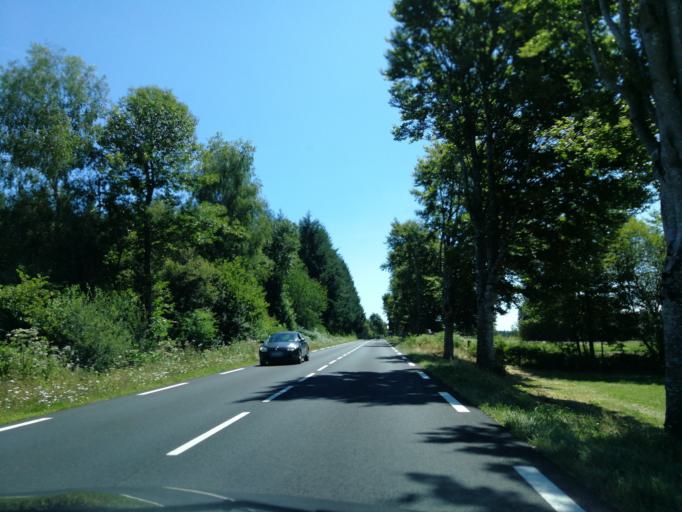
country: FR
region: Limousin
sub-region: Departement de la Correze
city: Saint-Privat
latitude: 45.0023
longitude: 2.0534
